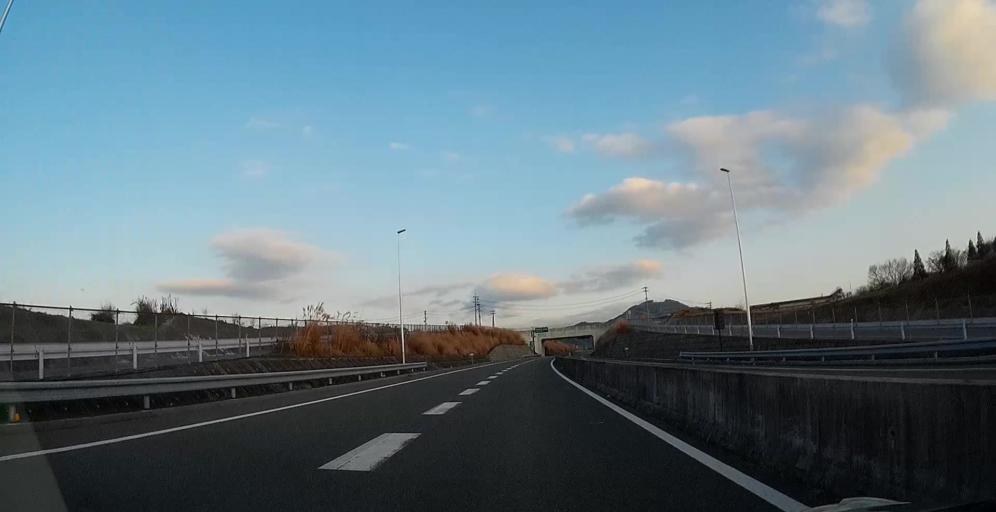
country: JP
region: Kumamoto
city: Kumamoto
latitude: 32.7538
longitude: 130.7914
